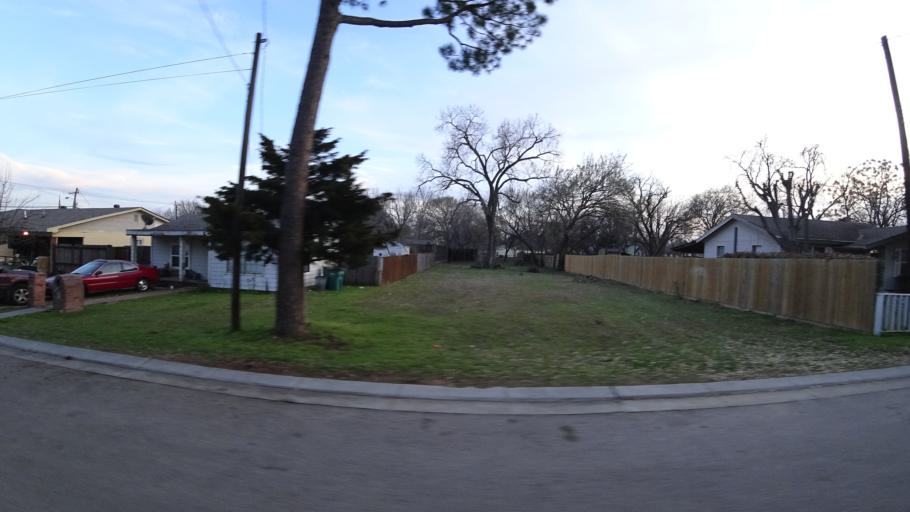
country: US
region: Texas
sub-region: Denton County
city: Lewisville
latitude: 33.0443
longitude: -96.9971
